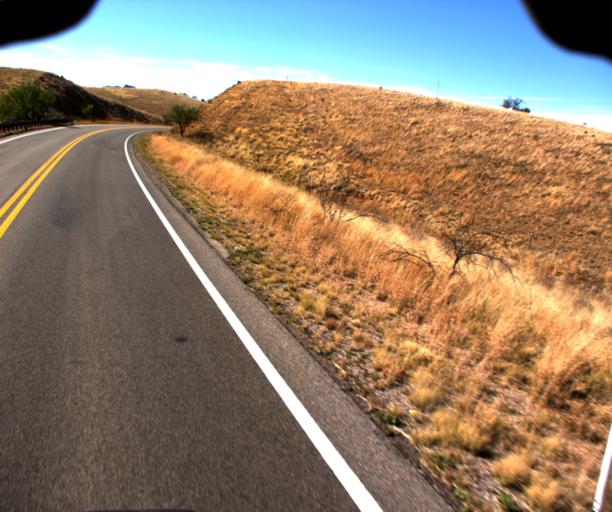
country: US
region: Arizona
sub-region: Pima County
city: Corona de Tucson
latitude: 31.8042
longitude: -110.7062
